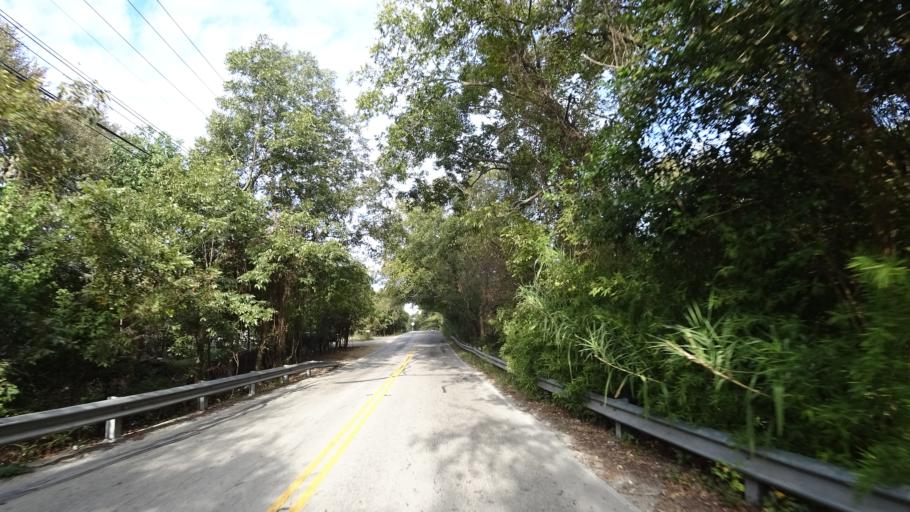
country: US
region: Texas
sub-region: Travis County
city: Austin
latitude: 30.2043
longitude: -97.7351
